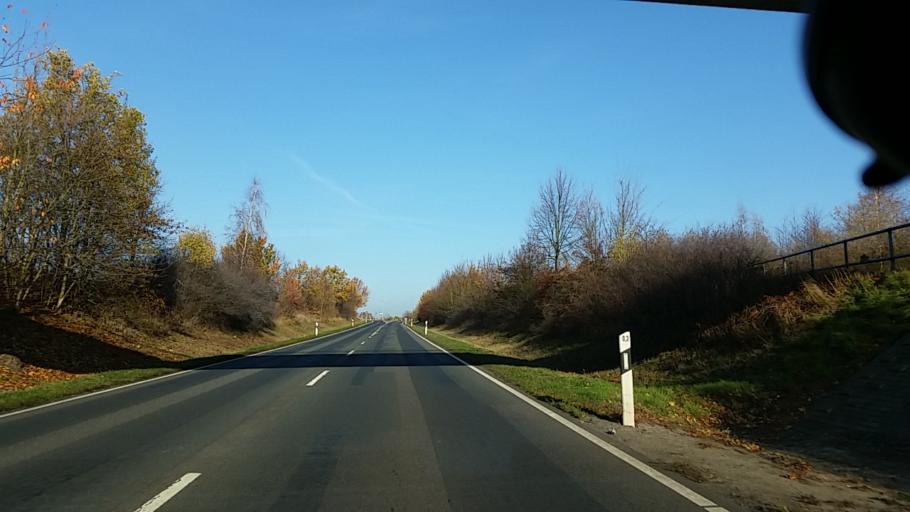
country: DE
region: Lower Saxony
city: Wolfsburg
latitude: 52.4420
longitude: 10.8254
